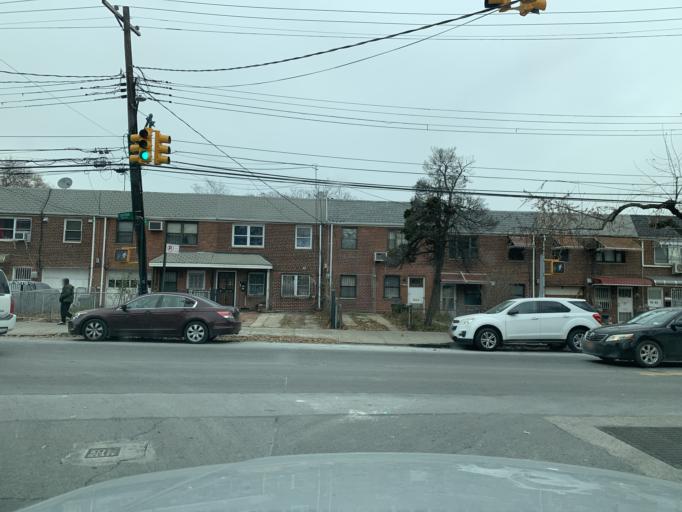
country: US
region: New York
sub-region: Queens County
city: Borough of Queens
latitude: 40.7389
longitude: -73.8669
